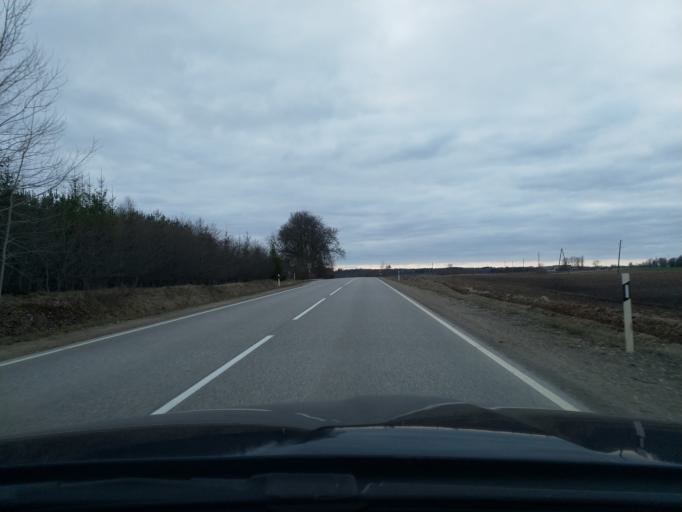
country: LV
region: Kuldigas Rajons
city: Kuldiga
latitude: 56.9634
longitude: 22.0691
